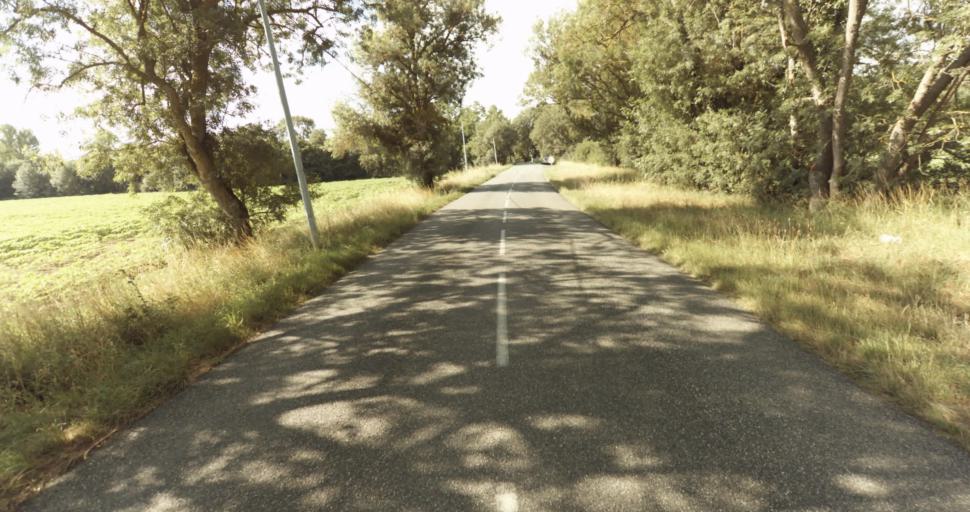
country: FR
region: Midi-Pyrenees
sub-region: Departement de la Haute-Garonne
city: Fonsorbes
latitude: 43.5649
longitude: 1.2335
